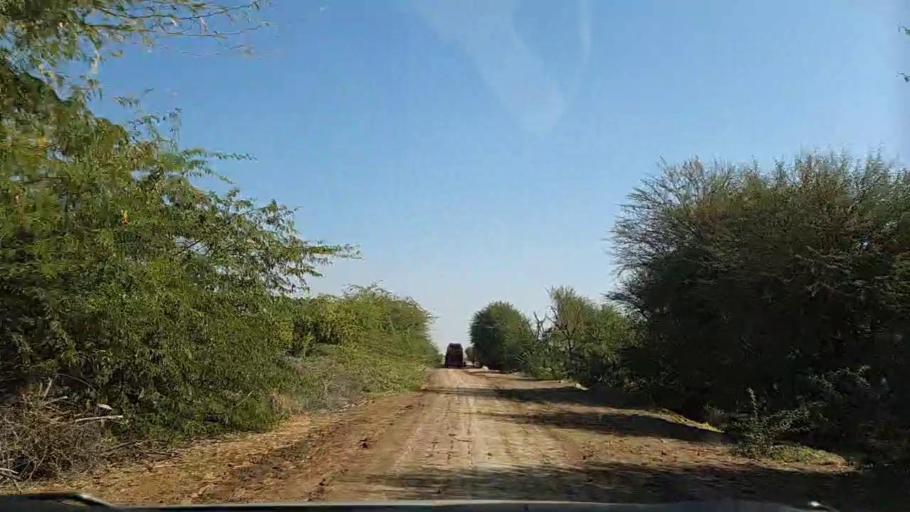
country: PK
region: Sindh
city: Pithoro
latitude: 25.6840
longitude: 69.3625
